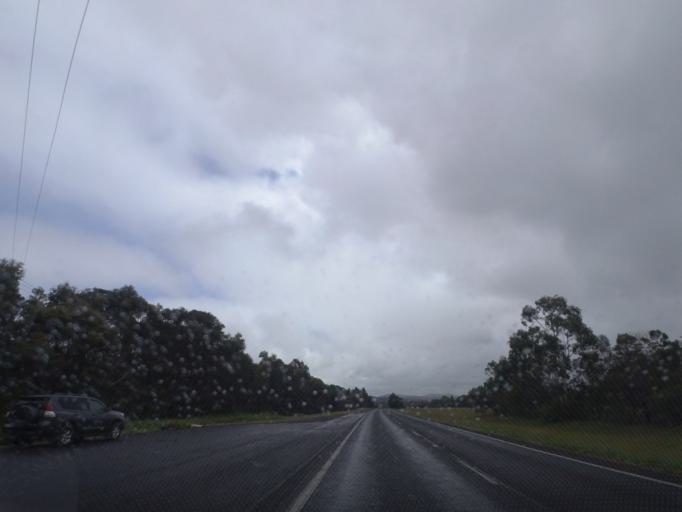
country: AU
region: Victoria
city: Black Hill
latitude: -37.5317
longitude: 143.8726
